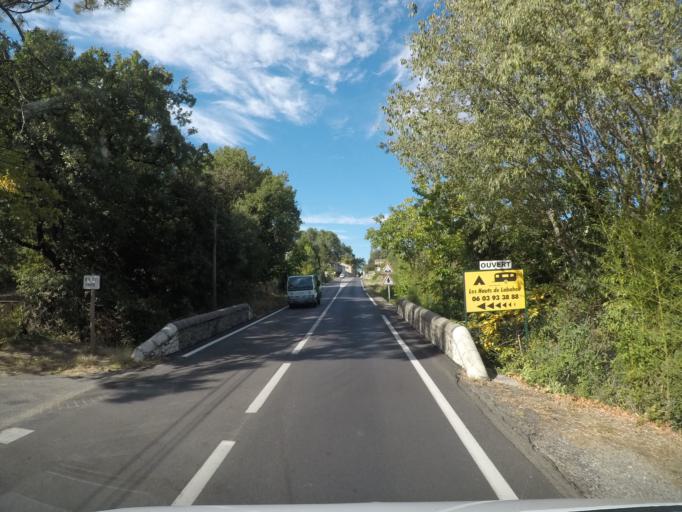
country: FR
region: Languedoc-Roussillon
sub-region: Departement du Gard
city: Anduze
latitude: 44.0696
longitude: 3.9696
